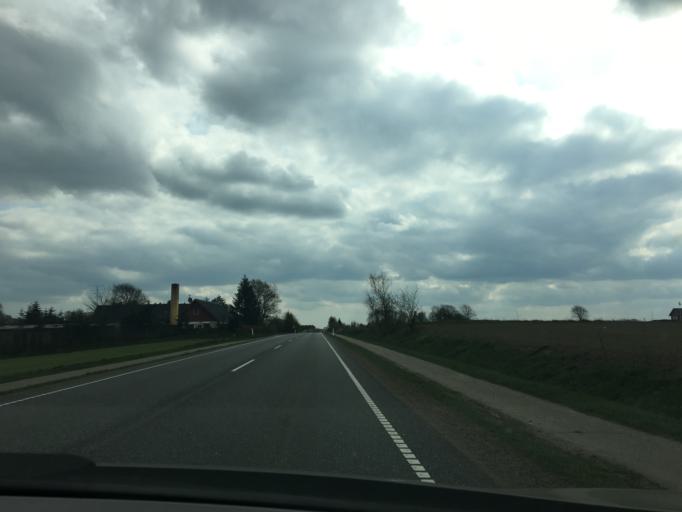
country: DK
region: Central Jutland
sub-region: Horsens Kommune
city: Braedstrup
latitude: 55.9900
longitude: 9.6043
